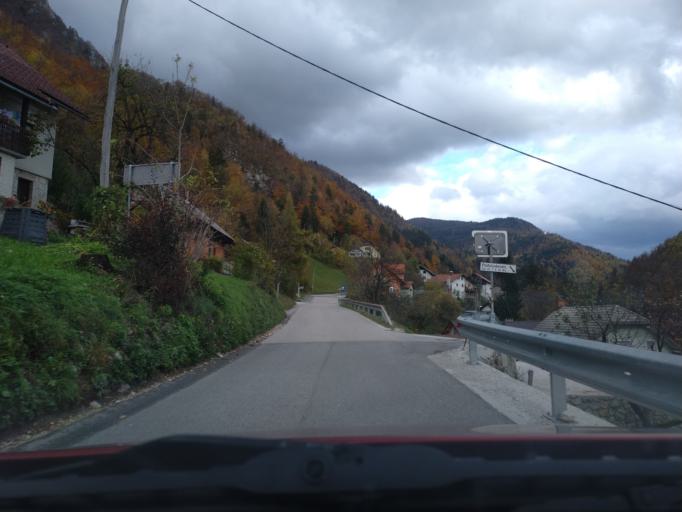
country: SI
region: Kamnik
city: Mekinje
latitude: 46.2634
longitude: 14.6515
